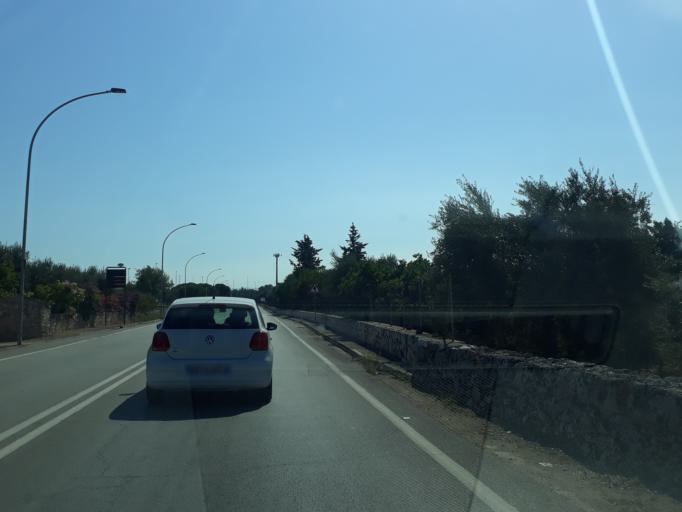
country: IT
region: Apulia
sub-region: Provincia di Bari
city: Monopoli
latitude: 40.9272
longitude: 17.3137
